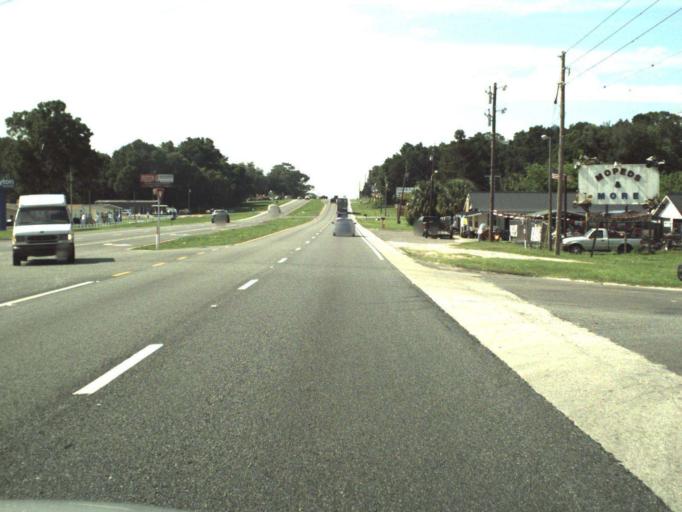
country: US
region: Florida
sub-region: Marion County
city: Ocala
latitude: 29.1244
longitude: -82.1016
